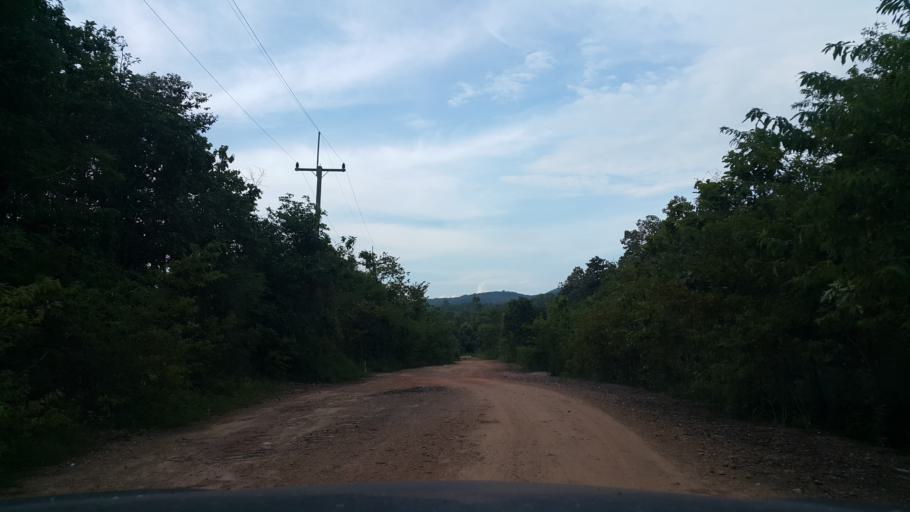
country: TH
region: Chiang Mai
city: San Sai
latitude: 18.9240
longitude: 99.0648
